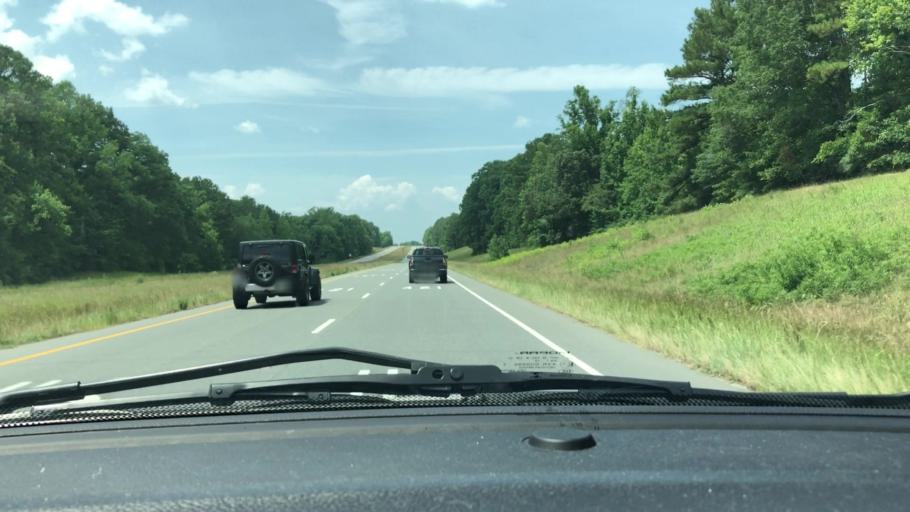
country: US
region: North Carolina
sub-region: Chatham County
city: Farmville
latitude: 35.5308
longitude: -79.2335
